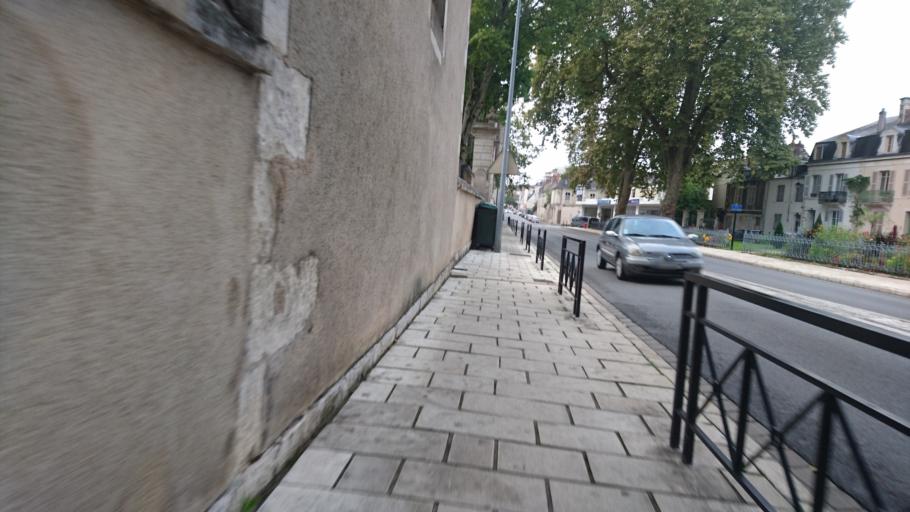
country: FR
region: Centre
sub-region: Departement du Cher
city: Bourges
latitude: 47.0905
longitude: 2.3936
